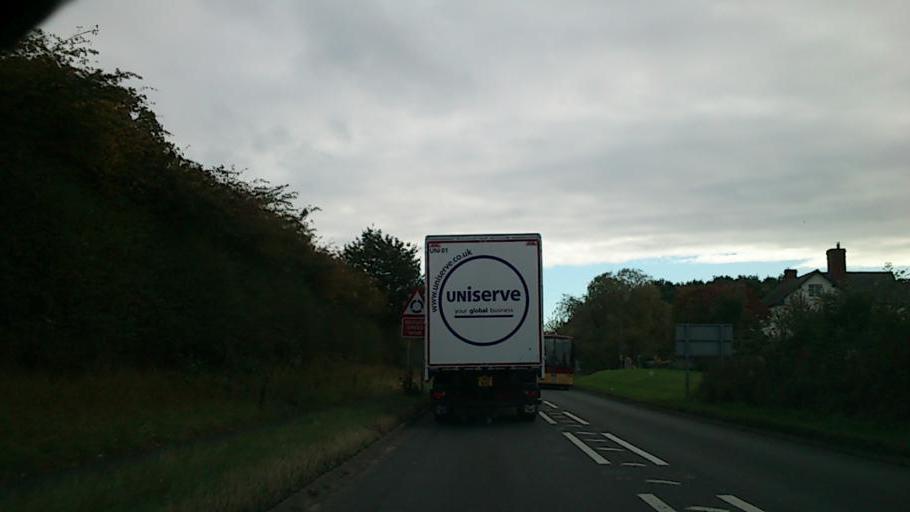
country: GB
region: England
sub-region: Shropshire
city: Bicton
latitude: 52.7163
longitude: -2.8252
